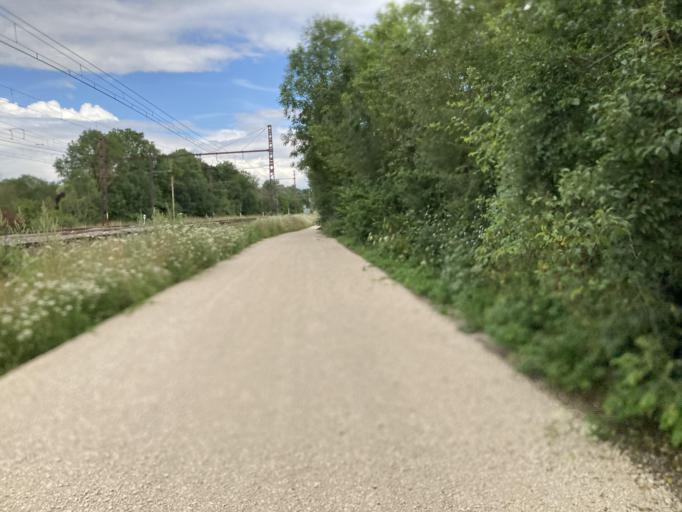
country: FR
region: Bourgogne
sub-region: Departement de la Cote-d'Or
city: Montbard
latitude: 47.6150
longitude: 4.3819
